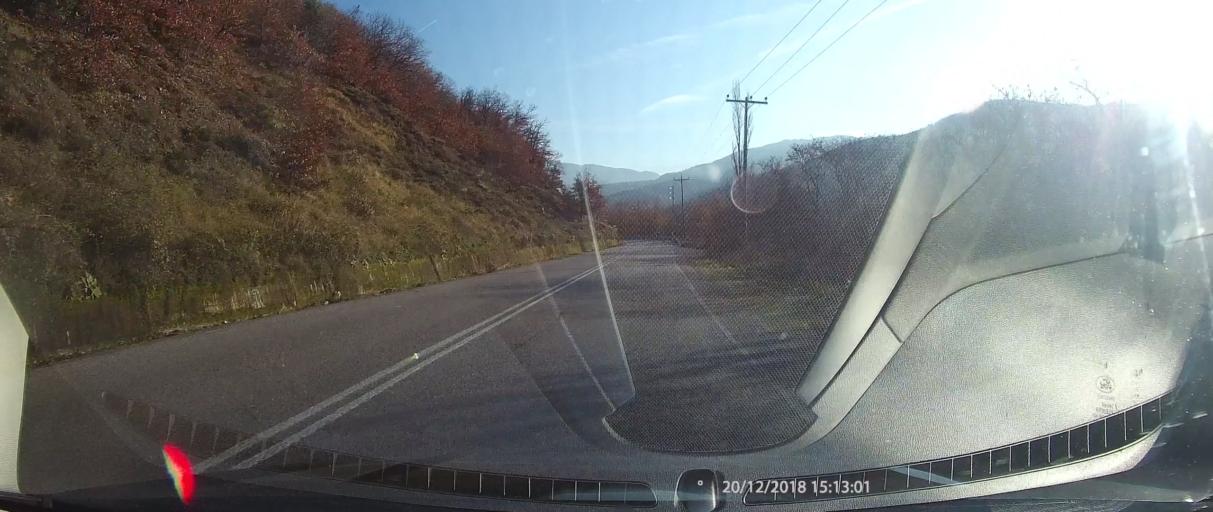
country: GR
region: Central Greece
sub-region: Nomos Fthiotidos
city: Makrakomi
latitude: 38.9371
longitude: 21.9645
